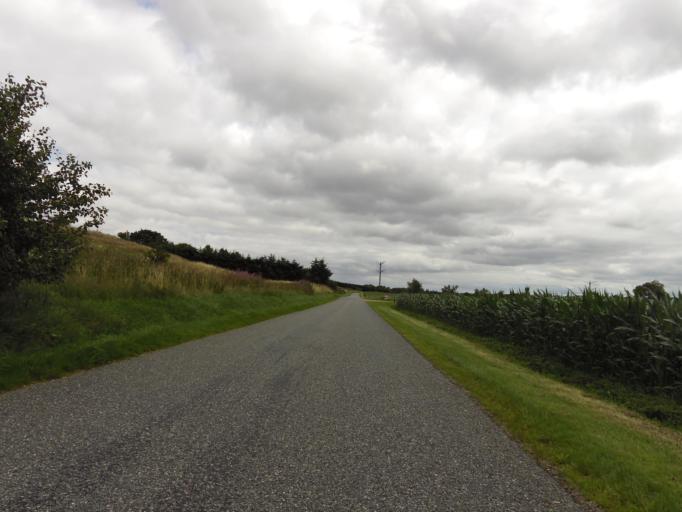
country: DK
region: South Denmark
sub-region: Haderslev Kommune
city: Gram
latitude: 55.3015
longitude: 9.1493
